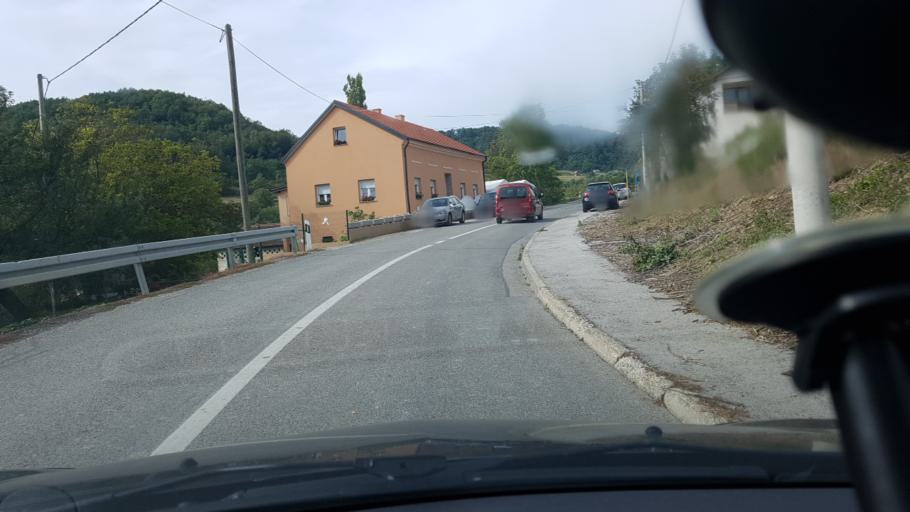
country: HR
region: Varazdinska
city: Ljubescica
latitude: 46.1048
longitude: 16.3588
